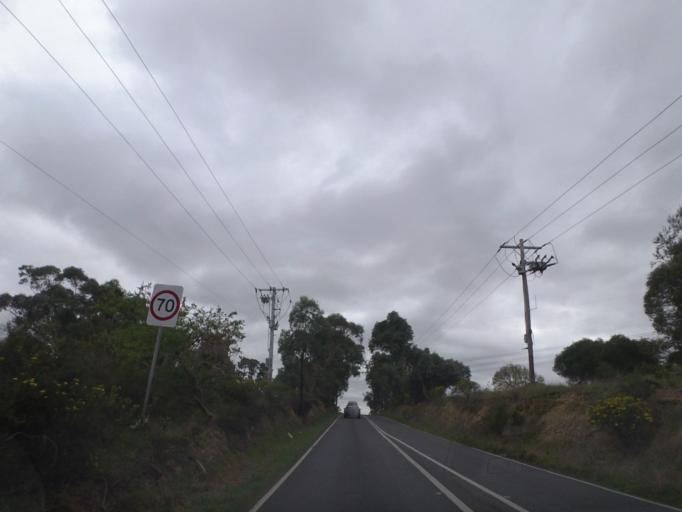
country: AU
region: Victoria
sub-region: Nillumbik
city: Eltham North
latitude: -37.6850
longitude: 145.1432
